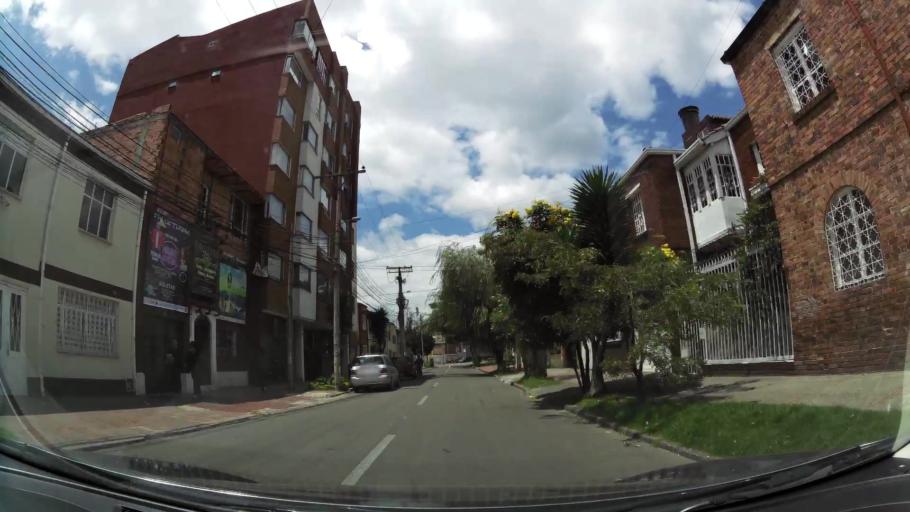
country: CO
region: Bogota D.C.
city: Bogota
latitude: 4.6345
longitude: -74.0725
